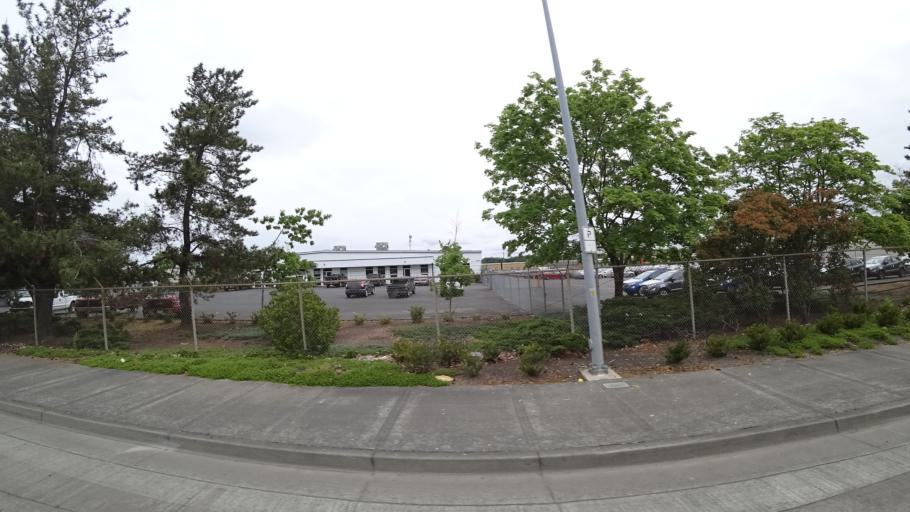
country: US
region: Washington
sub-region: Clark County
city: Vancouver
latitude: 45.6277
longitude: -122.7403
